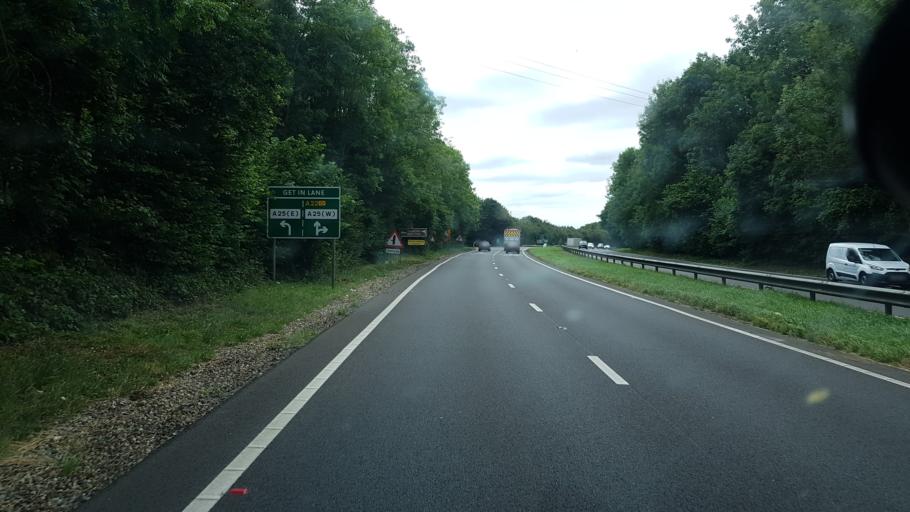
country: GB
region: England
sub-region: Surrey
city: Godstone
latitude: 51.2537
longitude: -0.0554
